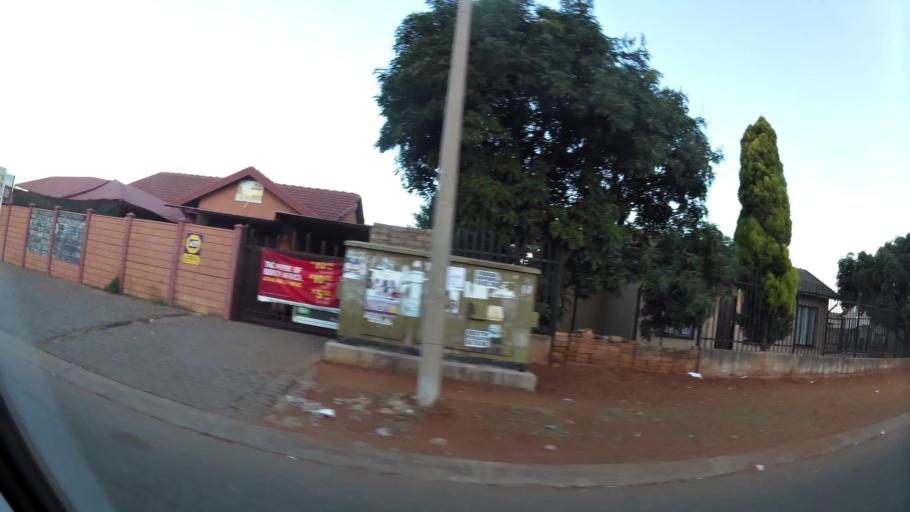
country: ZA
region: North-West
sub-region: Bojanala Platinum District Municipality
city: Rustenburg
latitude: -25.6500
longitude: 27.2086
